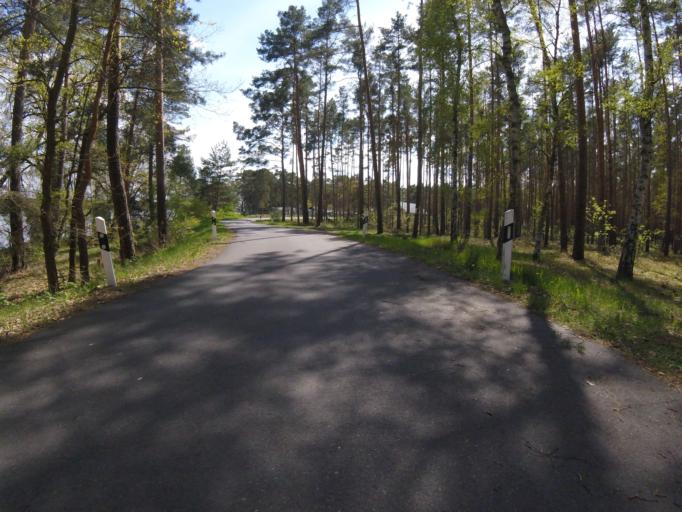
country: DE
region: Brandenburg
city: Gross Koris
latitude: 52.1983
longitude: 13.7075
